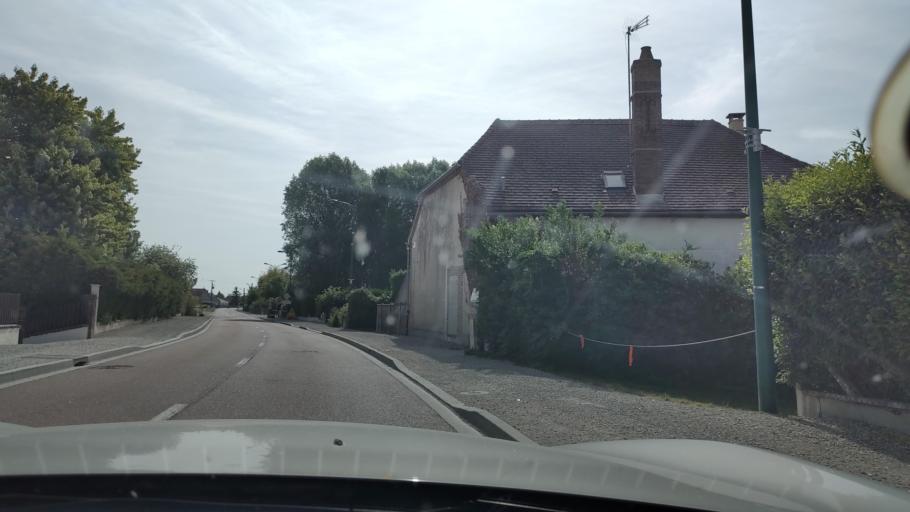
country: FR
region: Champagne-Ardenne
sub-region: Departement de l'Aube
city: Marigny-le-Chatel
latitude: 48.4018
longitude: 3.7450
